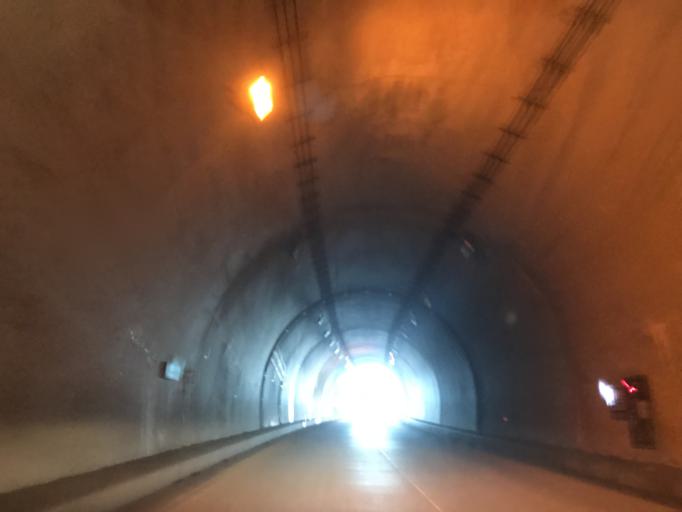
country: JP
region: Iwate
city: Mizusawa
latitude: 39.0289
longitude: 141.0207
